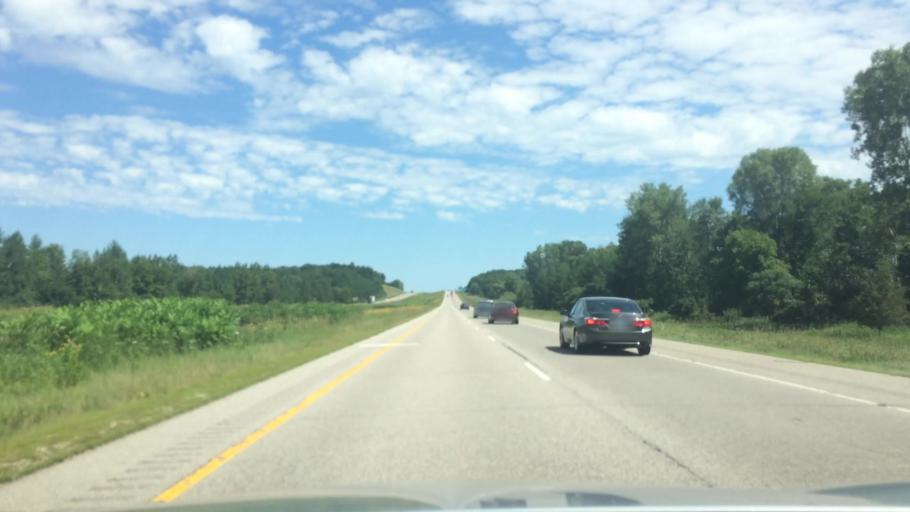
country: US
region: Wisconsin
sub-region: Marquette County
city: Westfield
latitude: 43.7740
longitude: -89.4843
